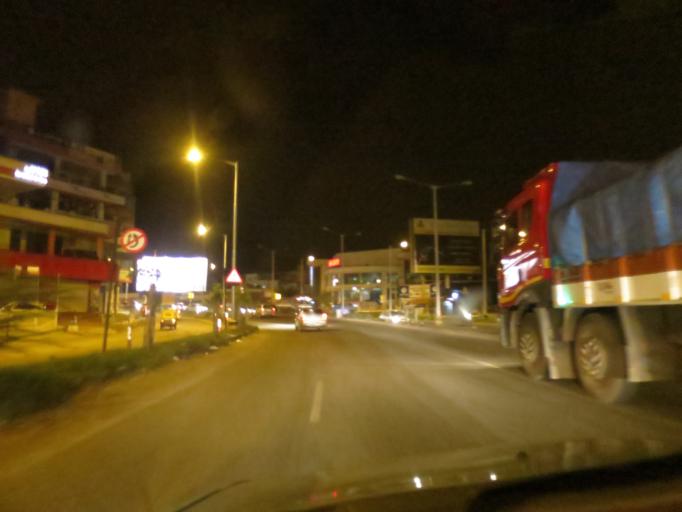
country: IN
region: Karnataka
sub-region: Bangalore Urban
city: Bangalore
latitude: 13.0157
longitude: 77.6620
